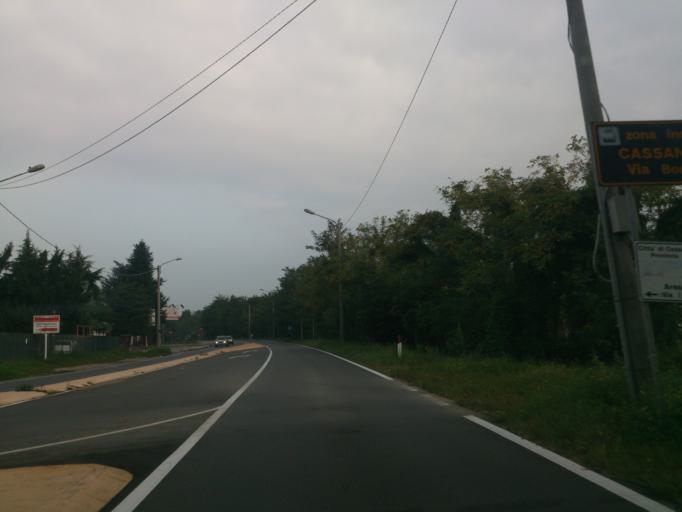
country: IT
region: Lombardy
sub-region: Provincia di Varese
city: Fagnano Olona-Bergoro
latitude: 45.6514
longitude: 8.8481
